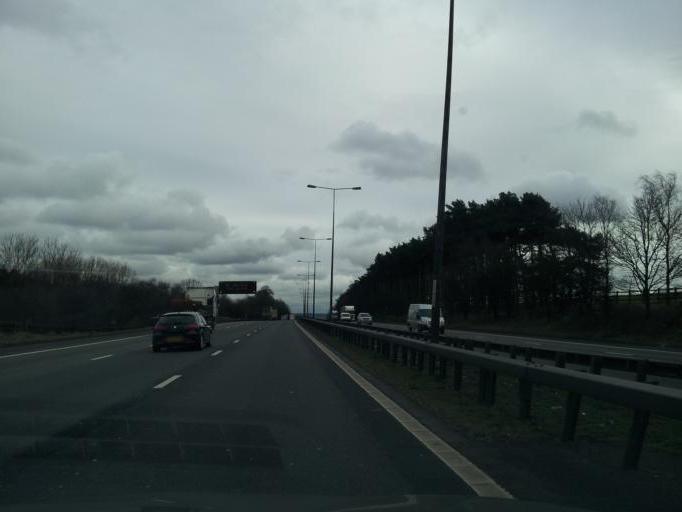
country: GB
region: England
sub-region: Staffordshire
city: Newcastle under Lyme
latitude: 52.9919
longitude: -2.2744
